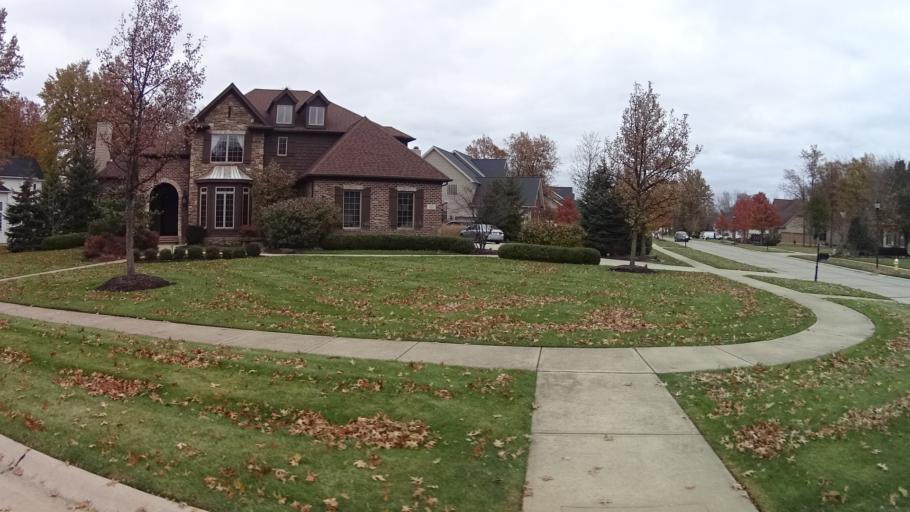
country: US
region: Ohio
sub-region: Lorain County
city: Avon Lake
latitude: 41.4877
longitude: -82.0043
